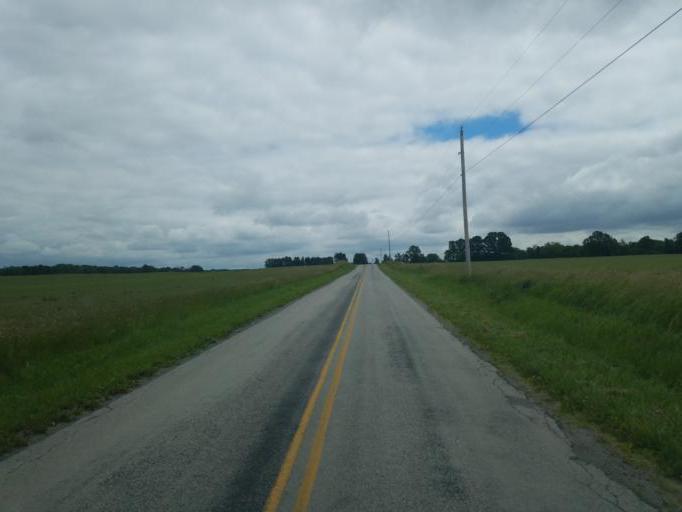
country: US
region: Ohio
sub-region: Wyandot County
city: Upper Sandusky
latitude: 40.7748
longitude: -83.1396
